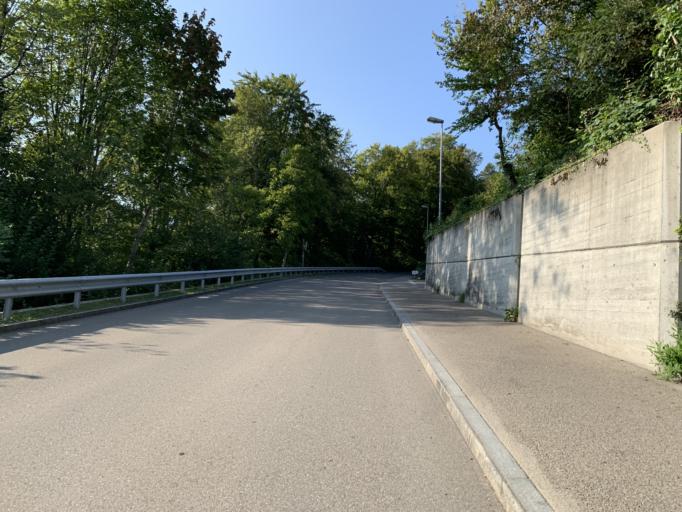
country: CH
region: Zurich
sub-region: Bezirk Hinwil
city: Hinwil
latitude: 47.3057
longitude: 8.8430
